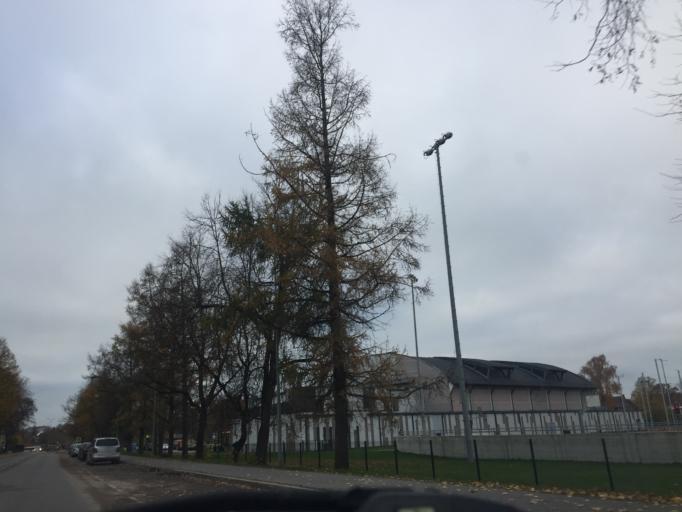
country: LV
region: Saldus Rajons
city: Saldus
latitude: 56.6671
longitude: 22.5005
